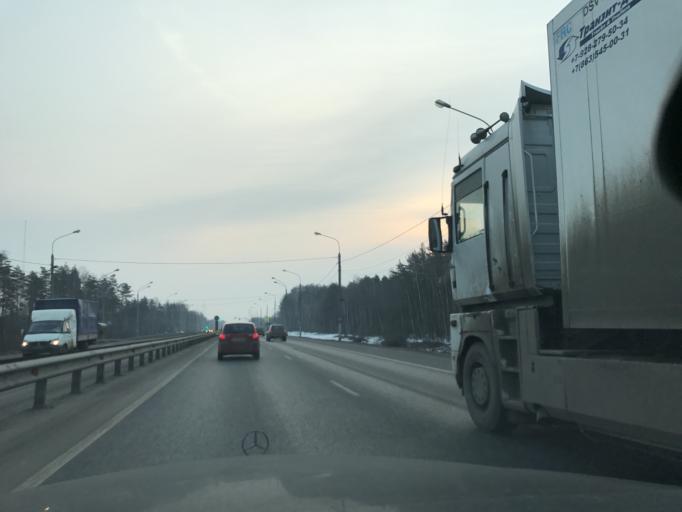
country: RU
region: Moskovskaya
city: Obukhovo
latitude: 55.8315
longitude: 38.3246
